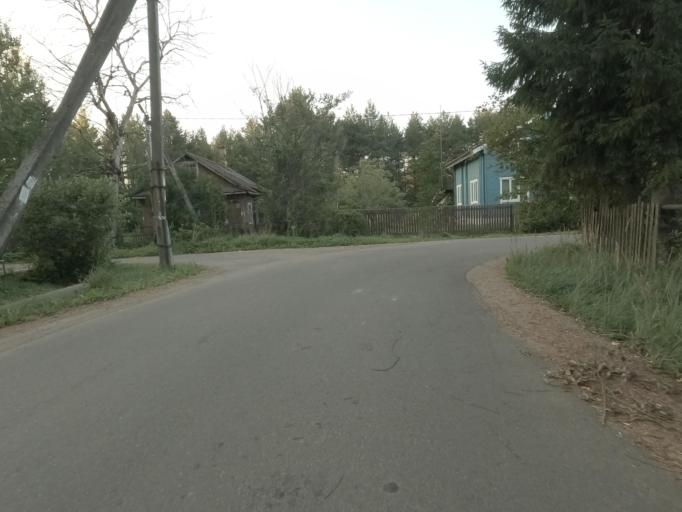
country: RU
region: Leningrad
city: Mga
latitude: 59.7612
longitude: 31.0471
